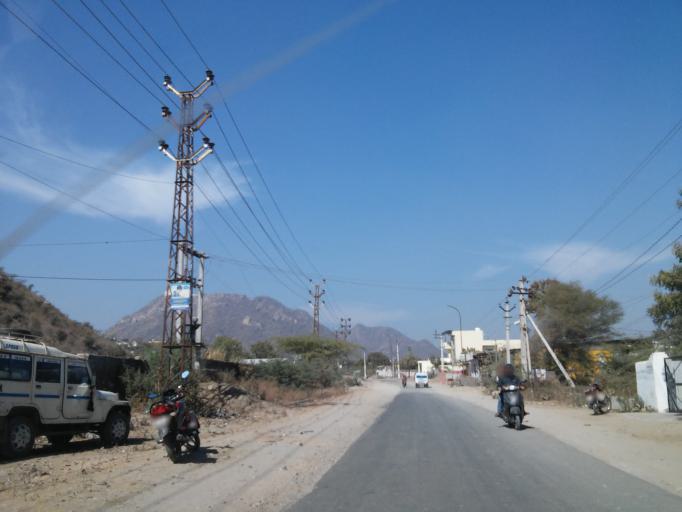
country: IN
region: Rajasthan
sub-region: Udaipur
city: Udaipur
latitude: 24.5787
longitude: 73.6545
